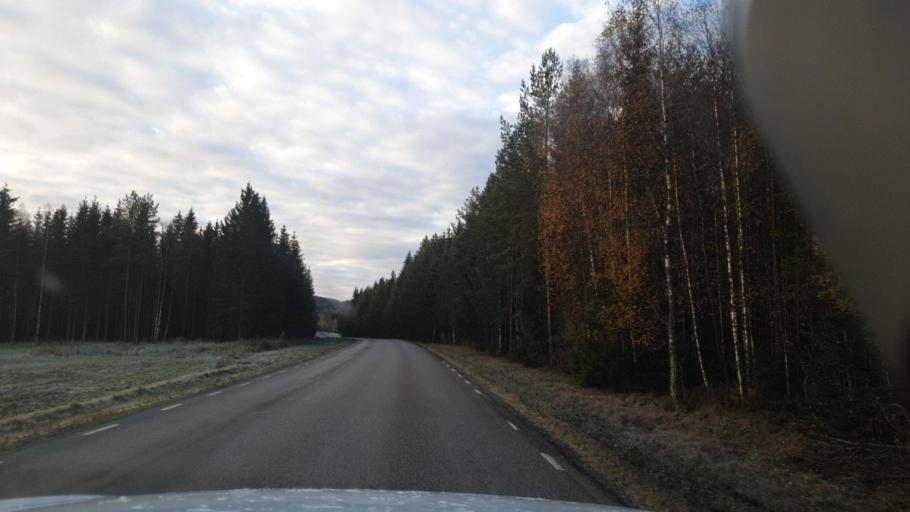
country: SE
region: Vaermland
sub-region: Eda Kommun
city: Charlottenberg
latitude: 59.7373
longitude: 12.1686
